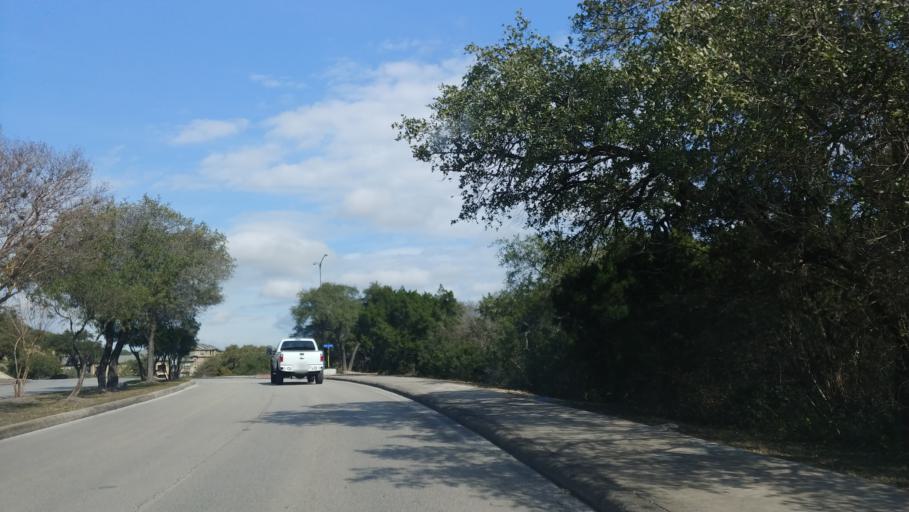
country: US
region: Texas
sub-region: Bexar County
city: Cross Mountain
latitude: 29.6192
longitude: -98.6112
